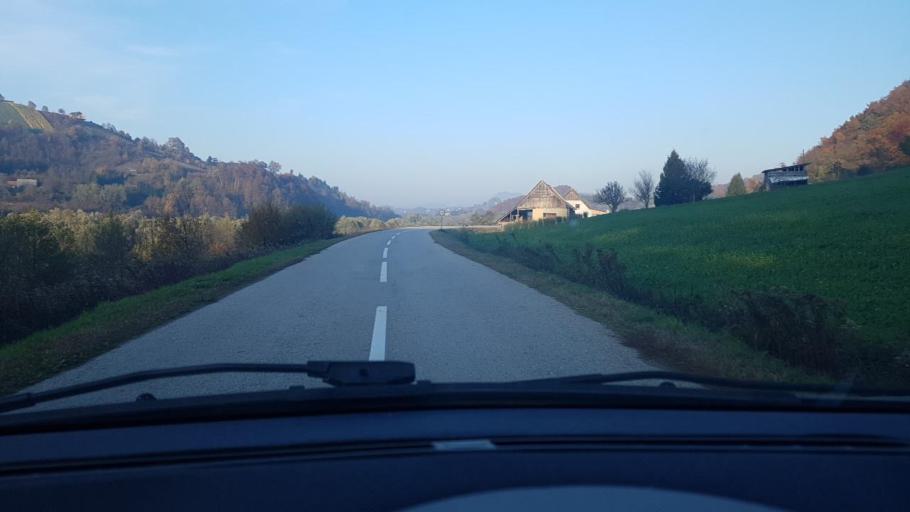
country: SI
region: Podcetrtek
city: Podcetrtek
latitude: 46.1735
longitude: 15.6279
